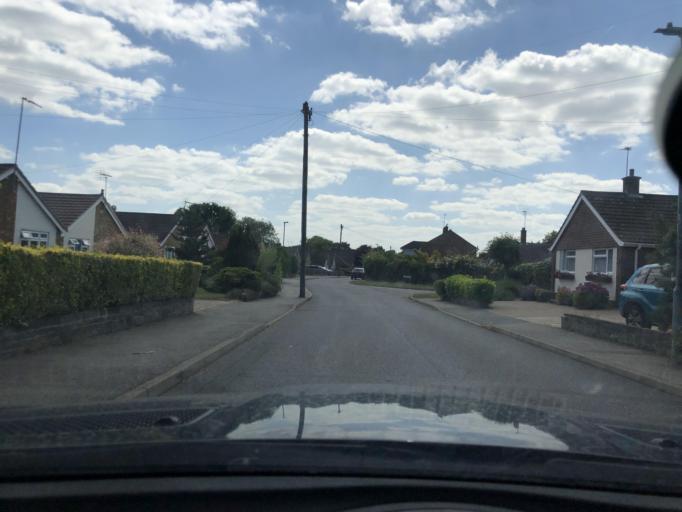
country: GB
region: England
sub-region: Essex
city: Chelmsford
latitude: 51.7459
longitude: 0.4966
